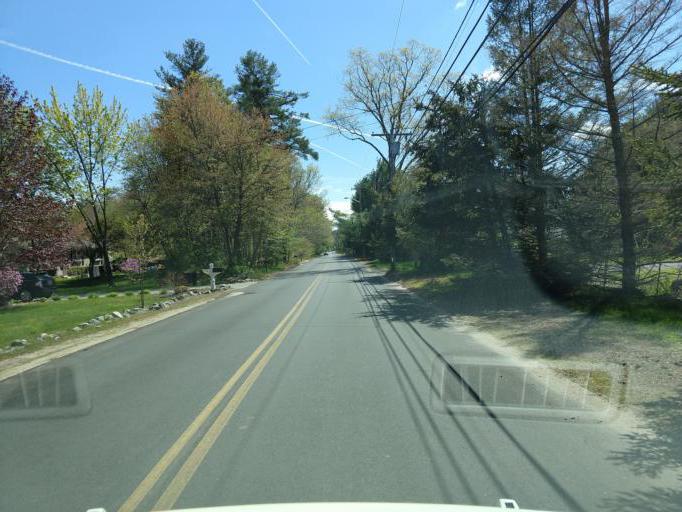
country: US
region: Massachusetts
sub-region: Essex County
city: Amesbury
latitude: 42.8803
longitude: -70.9070
